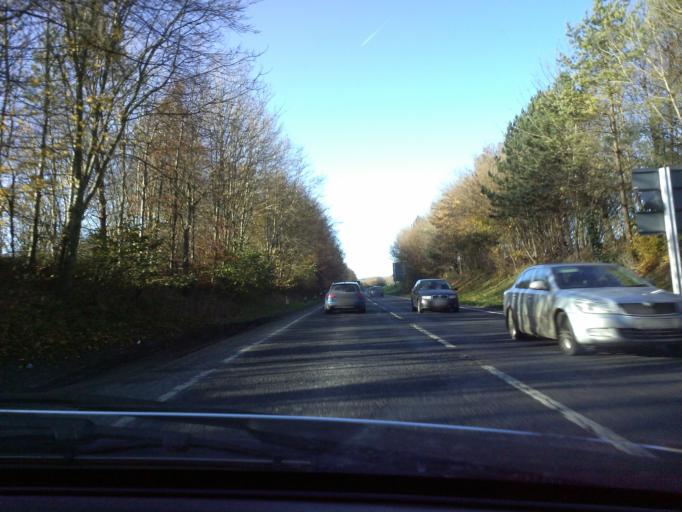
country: GB
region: England
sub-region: Dorset
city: Dorchester
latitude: 50.7005
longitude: -2.4496
